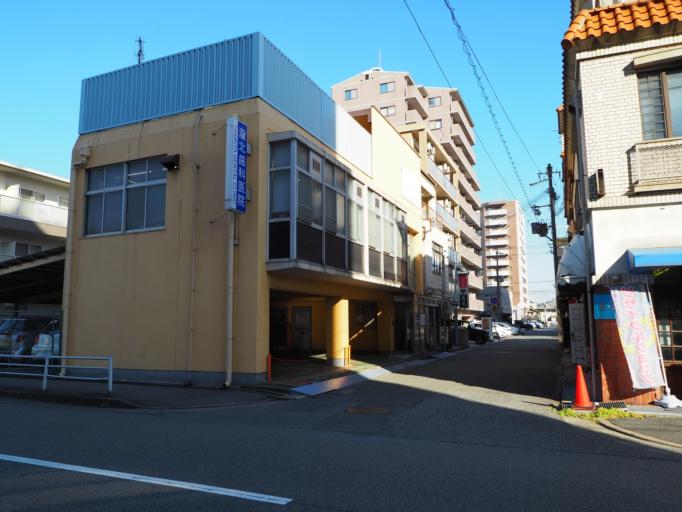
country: JP
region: Hyogo
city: Himeji
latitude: 34.8014
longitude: 134.6759
